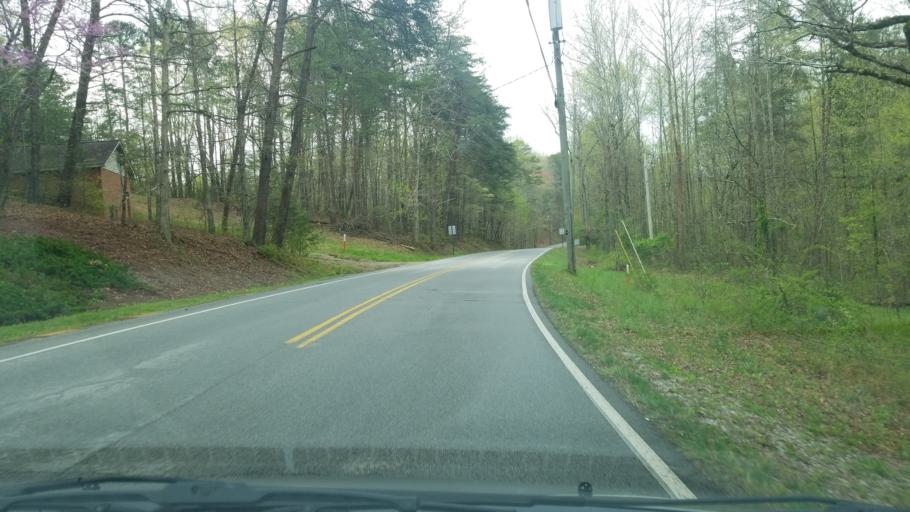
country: US
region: Tennessee
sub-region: Hamilton County
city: Collegedale
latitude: 35.0239
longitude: -85.0708
